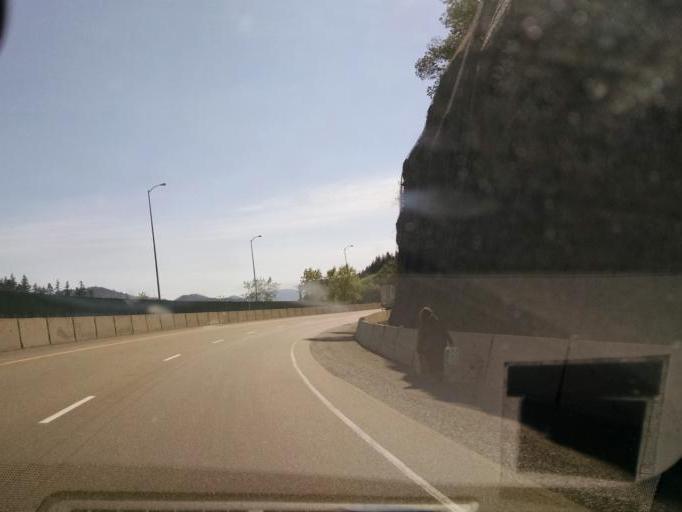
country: US
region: Oregon
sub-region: Douglas County
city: Myrtle Creek
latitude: 43.0237
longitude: -123.2978
